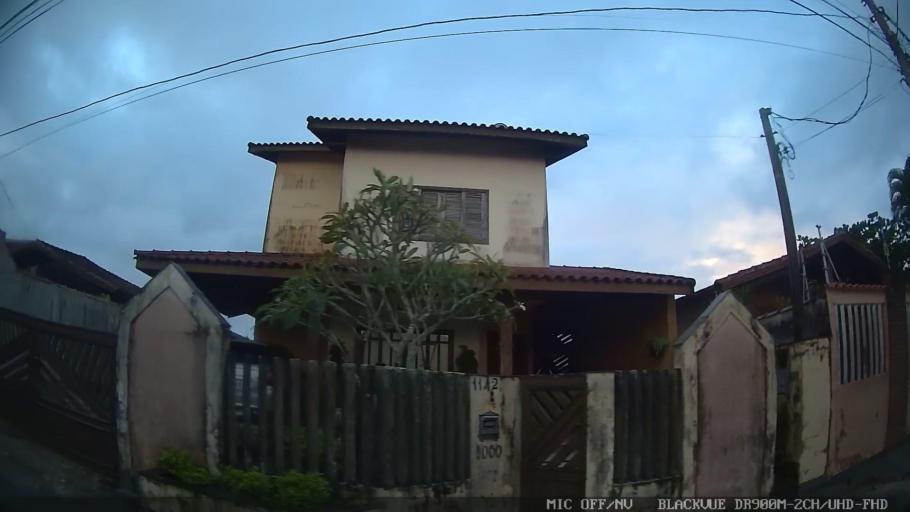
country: BR
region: Sao Paulo
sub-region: Itanhaem
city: Itanhaem
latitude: -24.2069
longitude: -46.8337
